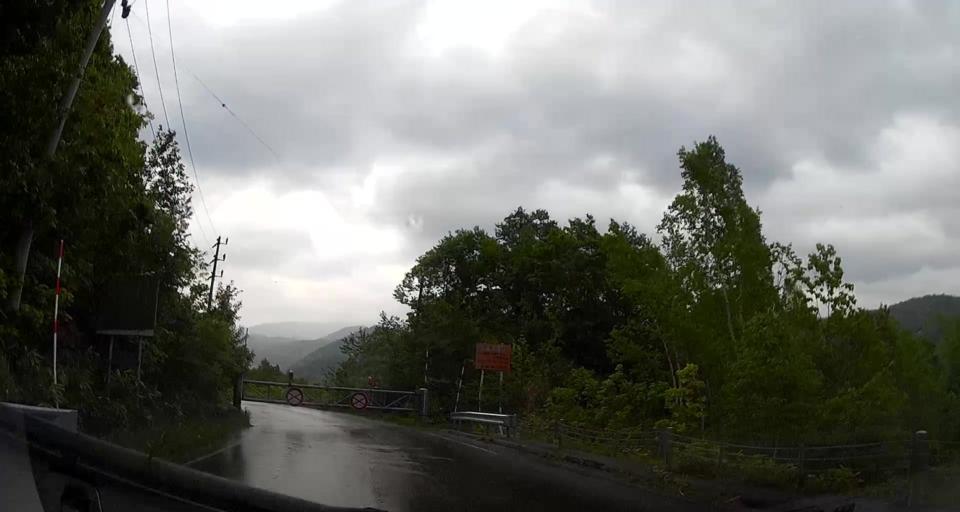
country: JP
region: Hokkaido
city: Otaru
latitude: 42.9154
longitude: 140.9359
